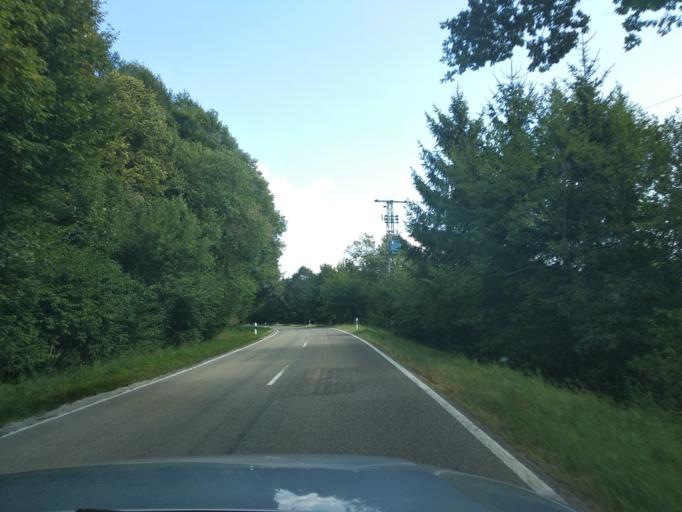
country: DE
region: Baden-Wuerttemberg
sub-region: Tuebingen Region
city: Leutkirch im Allgau
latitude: 47.8815
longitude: 9.9858
